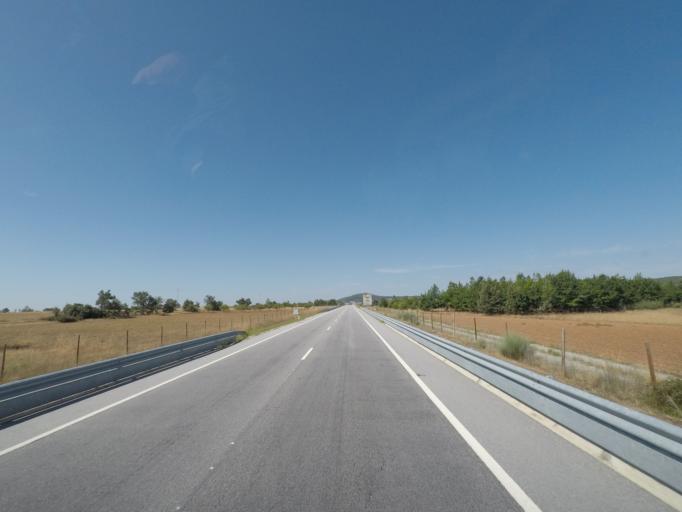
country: ES
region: Castille and Leon
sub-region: Provincia de Salamanca
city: Villarino de los Aires
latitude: 41.3589
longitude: -6.5571
